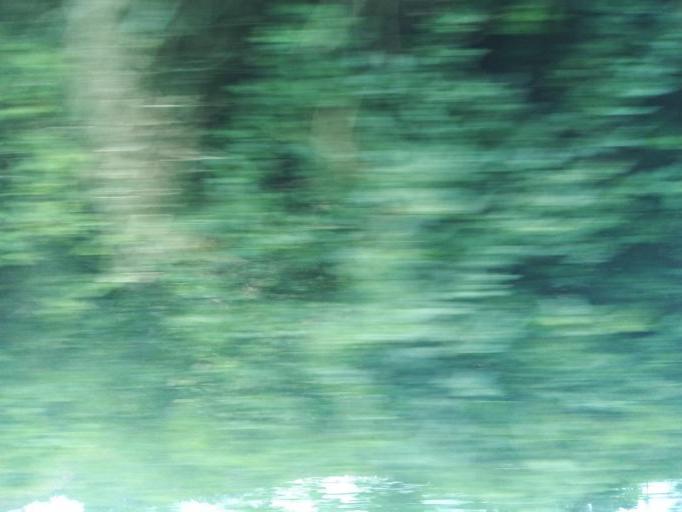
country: BR
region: Minas Gerais
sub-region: Timoteo
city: Timoteo
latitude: -19.5381
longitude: -42.6752
